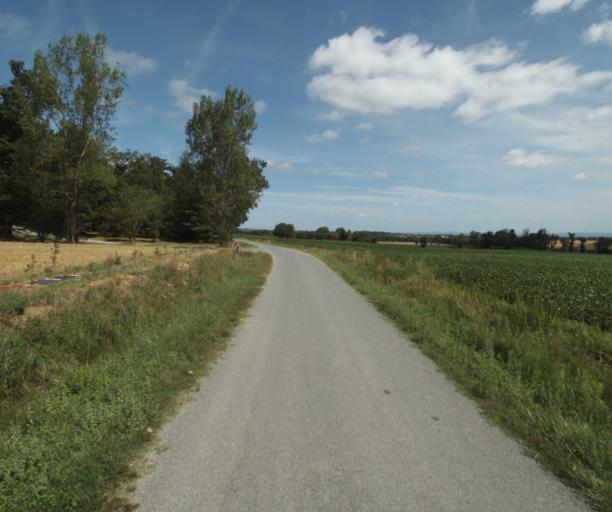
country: FR
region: Midi-Pyrenees
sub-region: Departement du Tarn
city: Soreze
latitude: 43.4788
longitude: 2.0766
